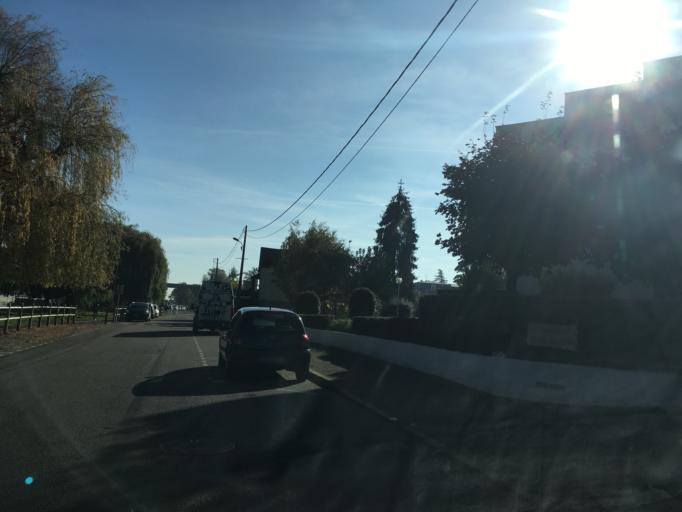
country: FR
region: Haute-Normandie
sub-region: Departement de l'Eure
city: Vernon
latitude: 49.0899
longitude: 1.4941
